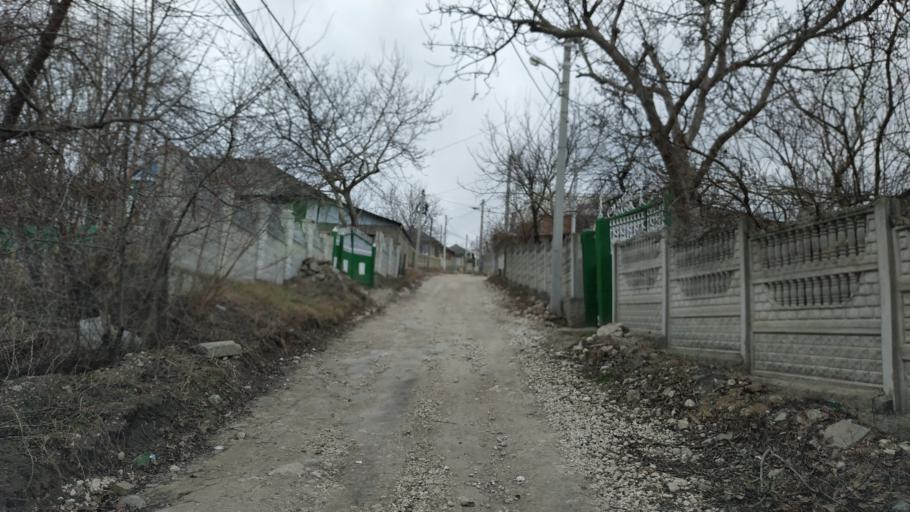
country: MD
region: Laloveni
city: Ialoveni
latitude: 46.9333
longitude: 28.7752
